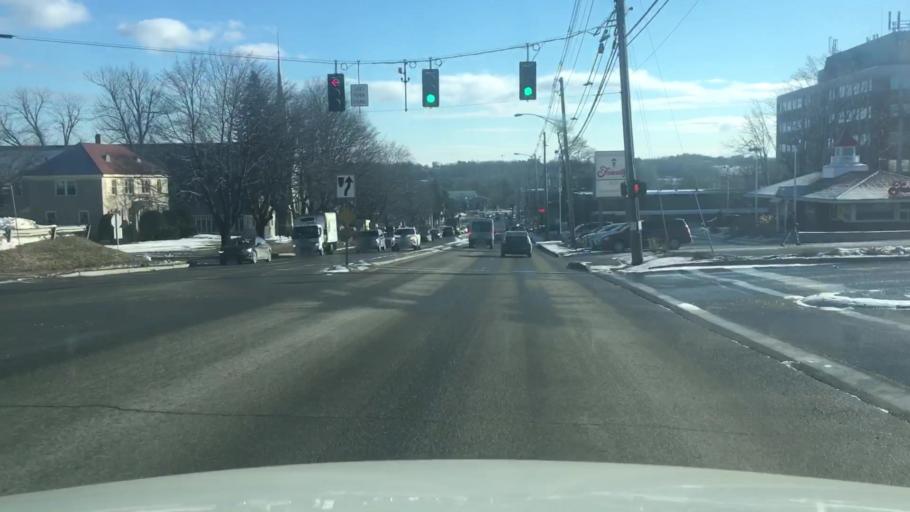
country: US
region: Maine
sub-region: Kennebec County
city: Augusta
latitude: 44.3115
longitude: -69.7855
